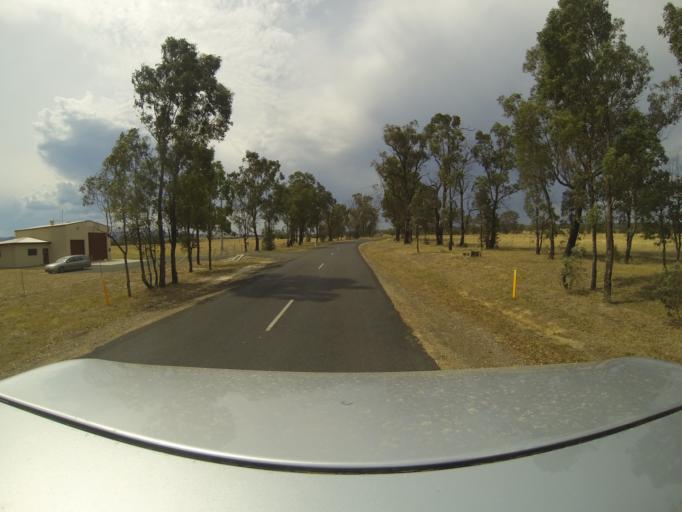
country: AU
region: Victoria
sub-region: Wellington
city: Heyfield
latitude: -37.9409
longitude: 146.6989
